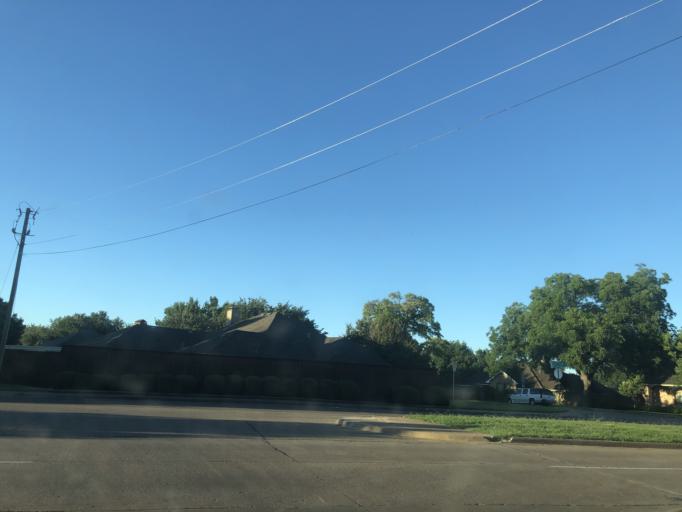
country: US
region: Texas
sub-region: Dallas County
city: Garland
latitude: 32.8379
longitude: -96.6456
